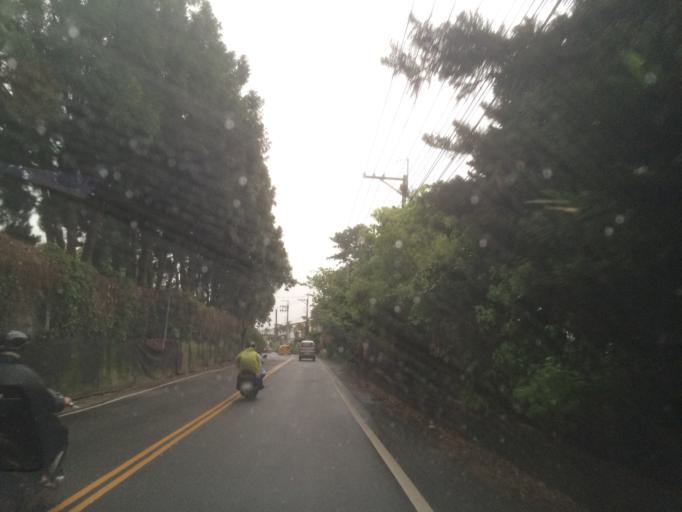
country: TW
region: Taiwan
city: Fengyuan
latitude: 24.1876
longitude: 120.8142
